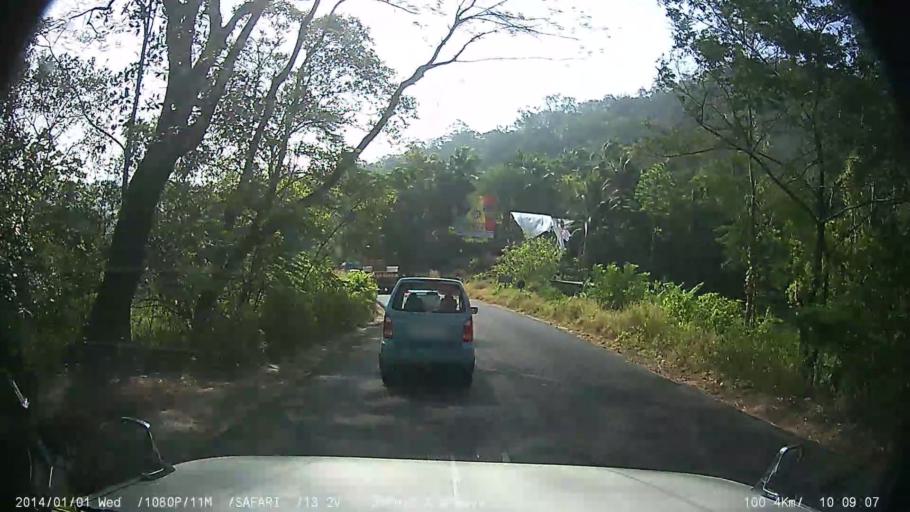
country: IN
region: Kerala
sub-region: Thrissur District
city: Chelakara
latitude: 10.5754
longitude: 76.3838
